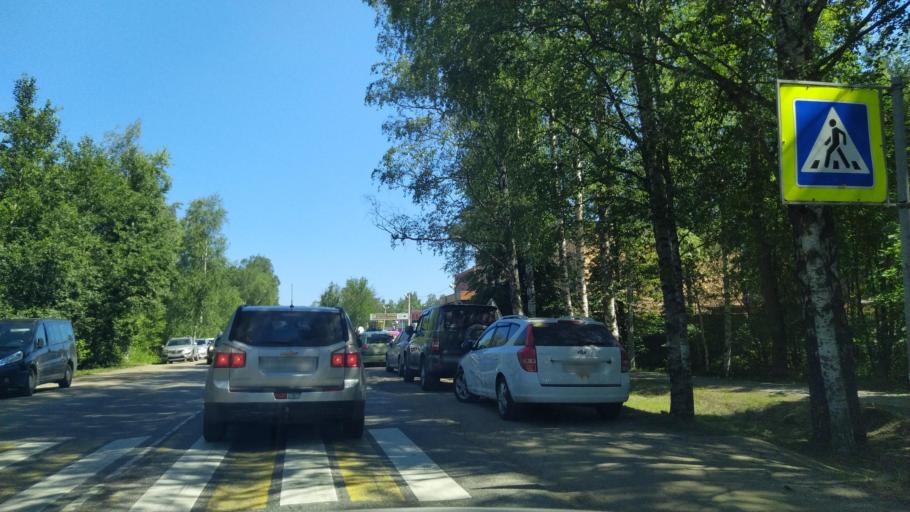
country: RU
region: Leningrad
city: Imeni Morozova
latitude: 59.9715
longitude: 31.0249
